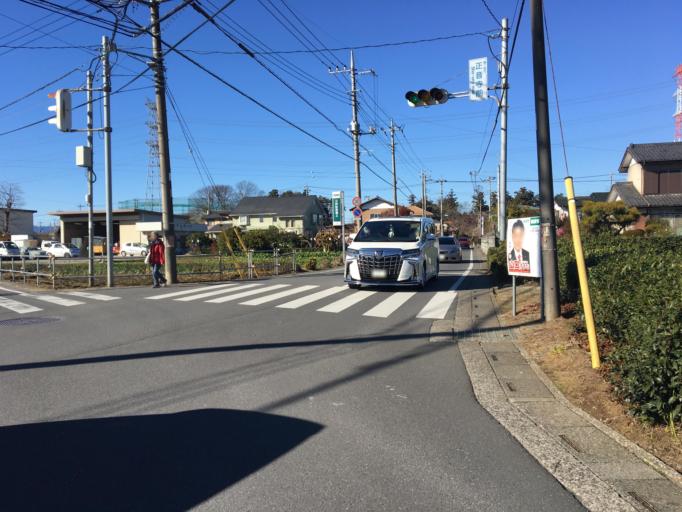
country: JP
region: Saitama
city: Sakado
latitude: 35.9405
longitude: 139.4156
